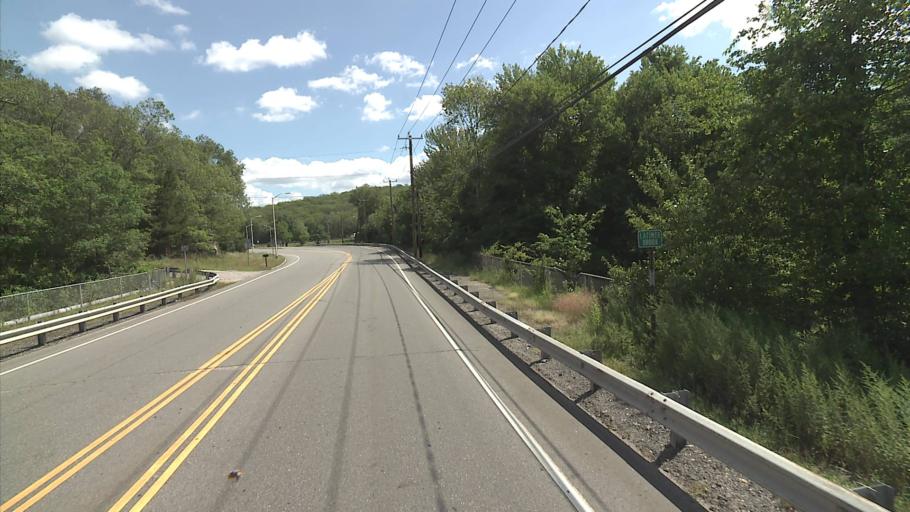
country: US
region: Connecticut
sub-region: New London County
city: Niantic
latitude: 41.3663
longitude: -72.2075
